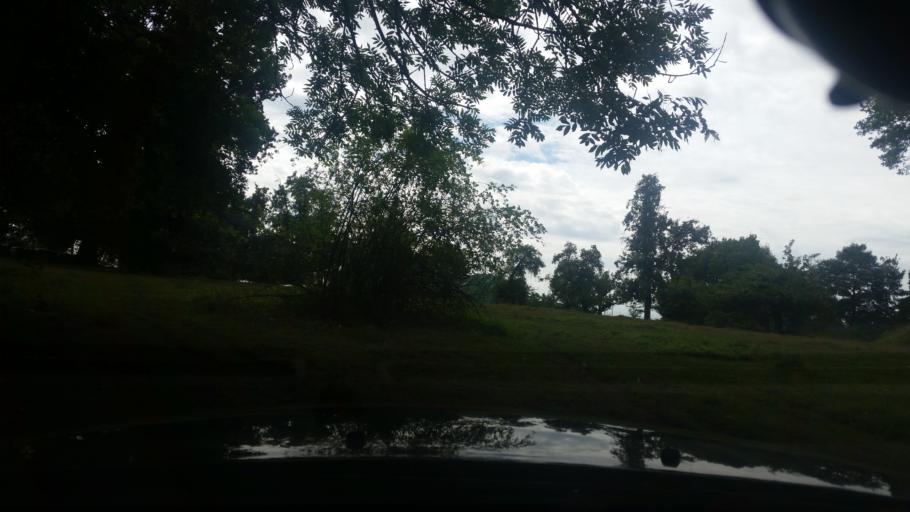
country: PL
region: Pomeranian Voivodeship
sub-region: Powiat leborski
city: Leba
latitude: 54.7260
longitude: 17.6196
